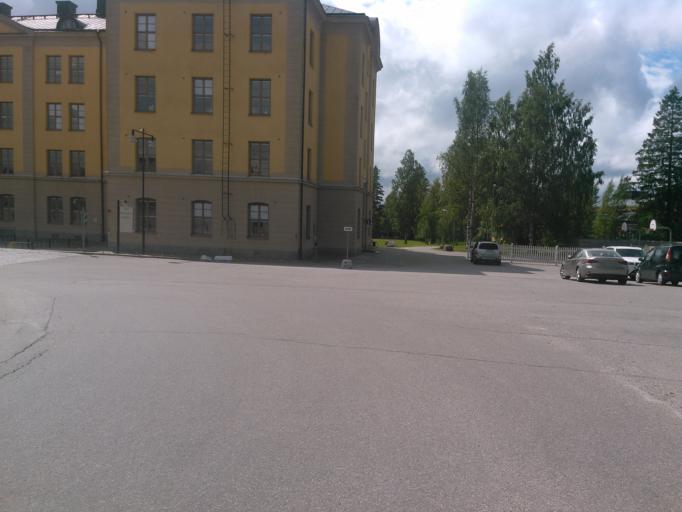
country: SE
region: Vaesterbotten
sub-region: Umea Kommun
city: Umea
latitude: 63.8355
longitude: 20.2594
